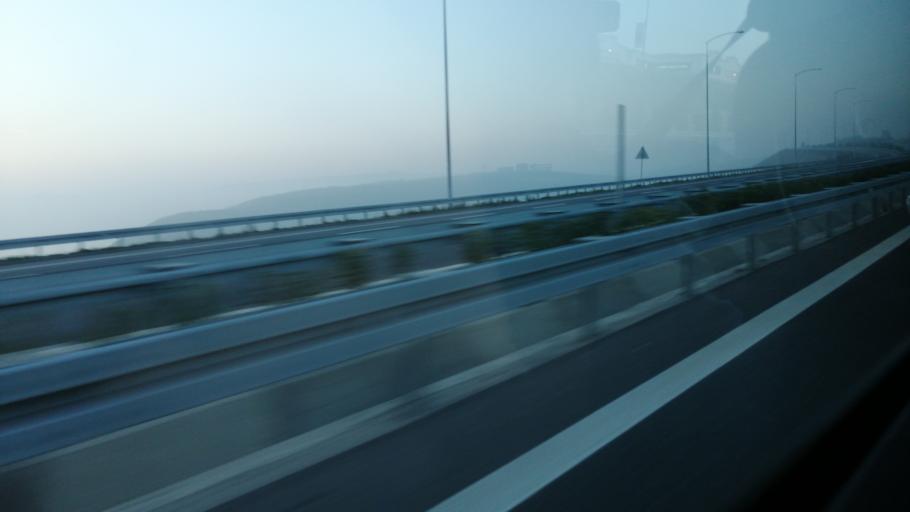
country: TR
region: Kocaeli
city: Tavsanli
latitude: 40.7716
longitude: 29.5185
